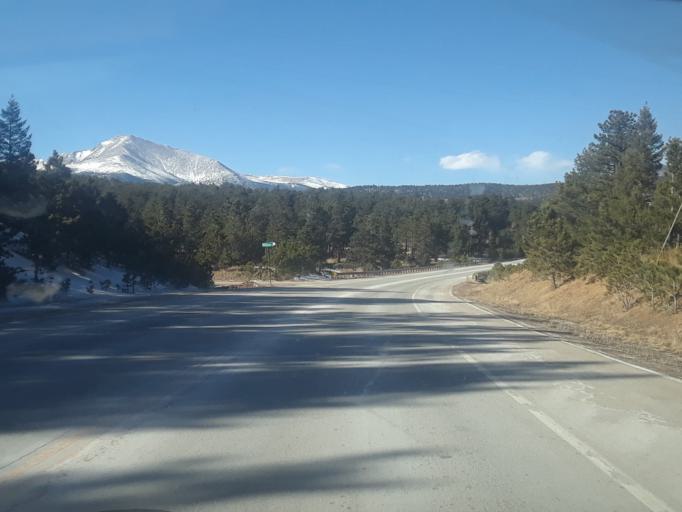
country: US
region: Colorado
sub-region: Boulder County
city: Lyons
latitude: 40.1737
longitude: -105.4686
